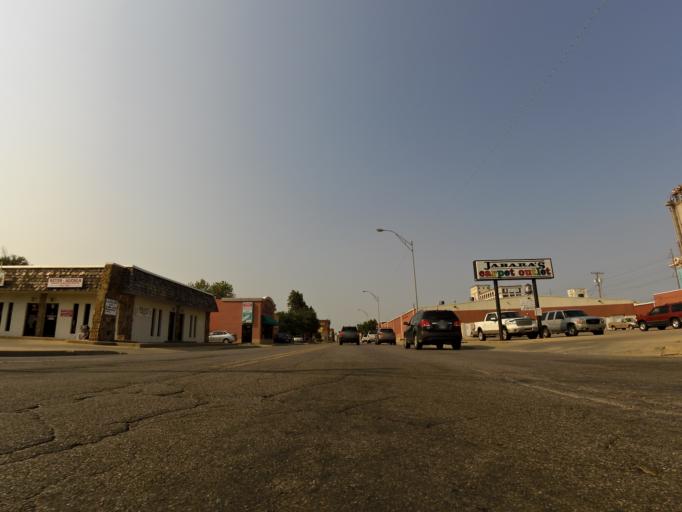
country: US
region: Kansas
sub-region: Sedgwick County
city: Wichita
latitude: 37.7154
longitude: -97.3356
